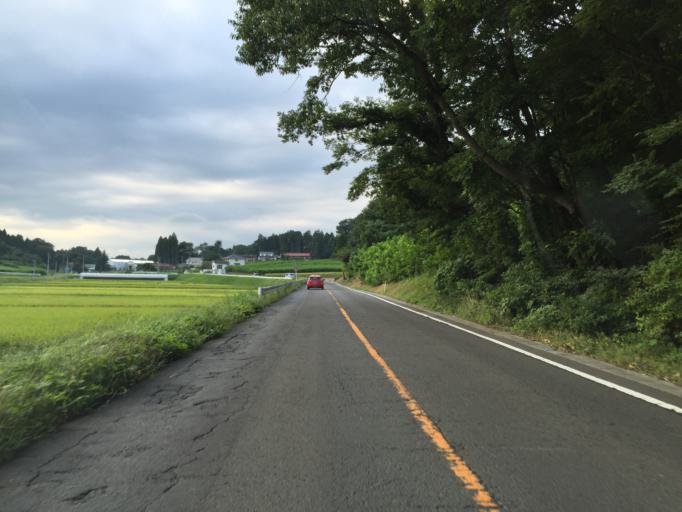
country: JP
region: Fukushima
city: Fukushima-shi
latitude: 37.6623
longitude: 140.5280
